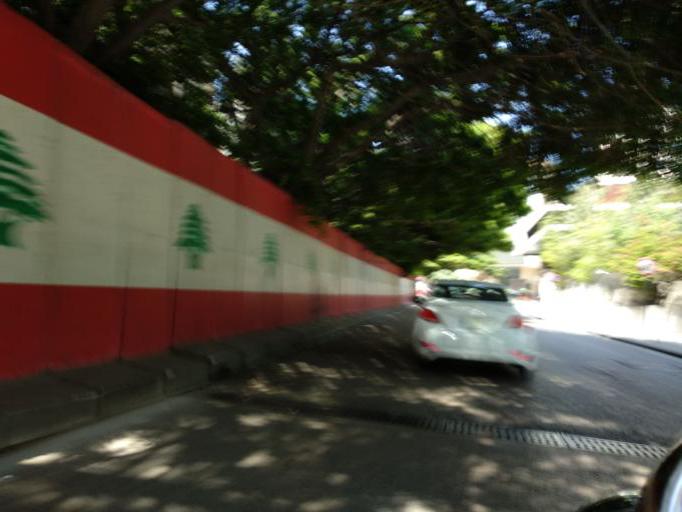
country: LB
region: Beyrouth
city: Beirut
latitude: 33.8958
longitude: 35.4958
